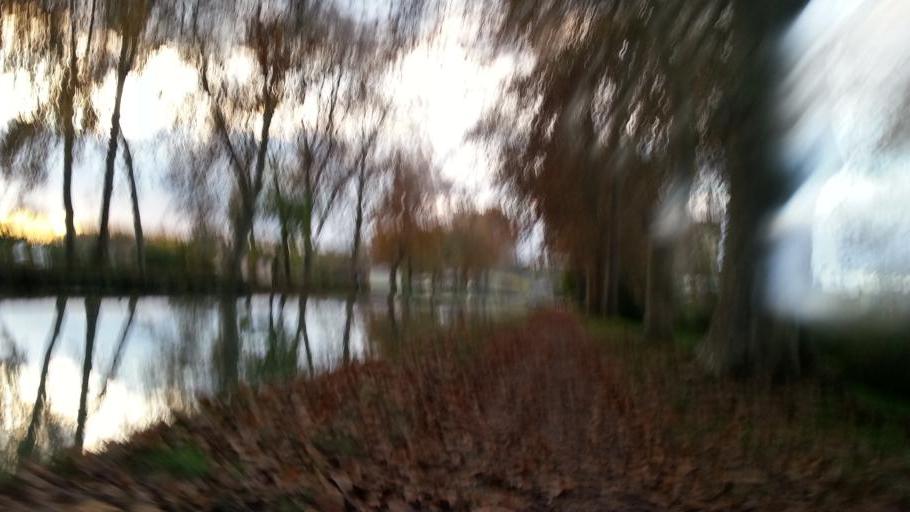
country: FR
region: Midi-Pyrenees
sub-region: Departement du Tarn-et-Garonne
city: Moissac
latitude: 44.0991
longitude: 1.0955
